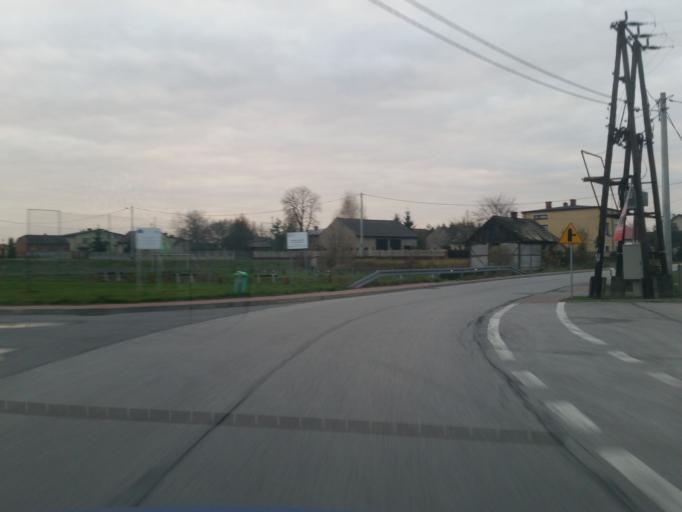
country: PL
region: Silesian Voivodeship
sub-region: Powiat czestochowski
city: Borowno
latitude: 50.9563
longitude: 19.2595
